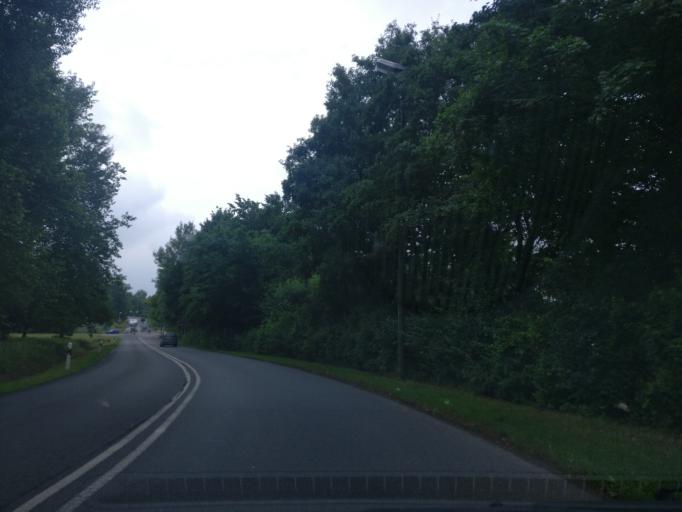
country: DE
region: Lower Saxony
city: Goettingen
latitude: 51.5576
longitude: 9.9416
